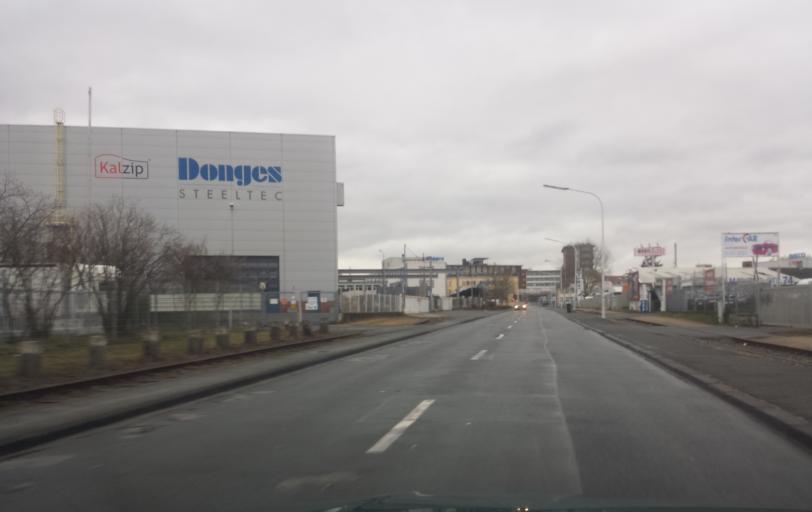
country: DE
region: Hesse
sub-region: Regierungsbezirk Darmstadt
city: Darmstadt
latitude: 49.8809
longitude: 8.6324
